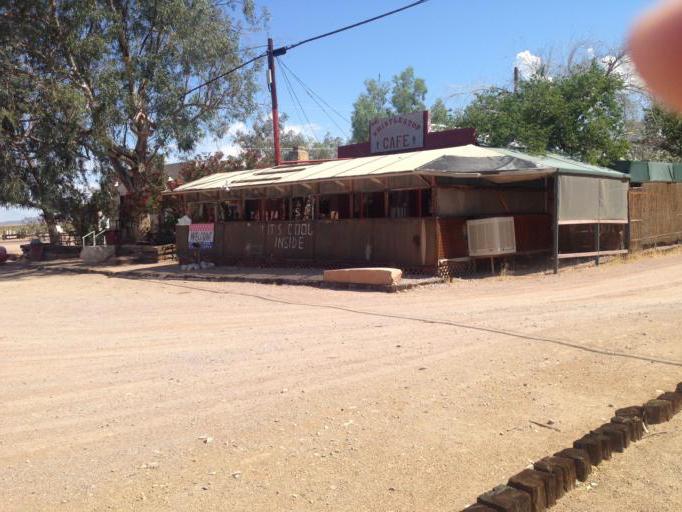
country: US
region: Nevada
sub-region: Clark County
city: Sandy Valley
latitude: 35.4668
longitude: -115.2719
